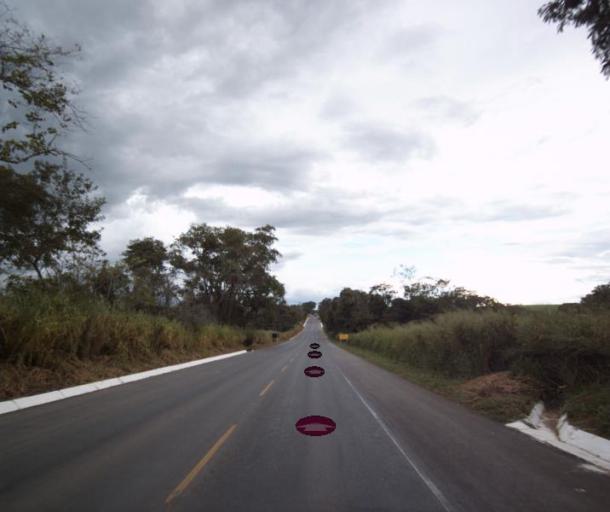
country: BR
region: Goias
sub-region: Itapaci
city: Itapaci
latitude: -14.9871
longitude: -49.4022
